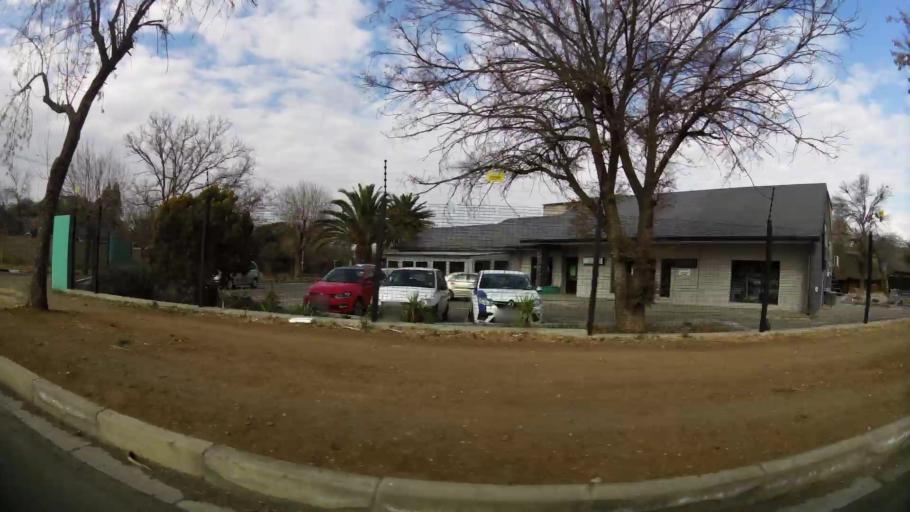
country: ZA
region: Orange Free State
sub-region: Mangaung Metropolitan Municipality
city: Bloemfontein
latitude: -29.0818
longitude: 26.2344
